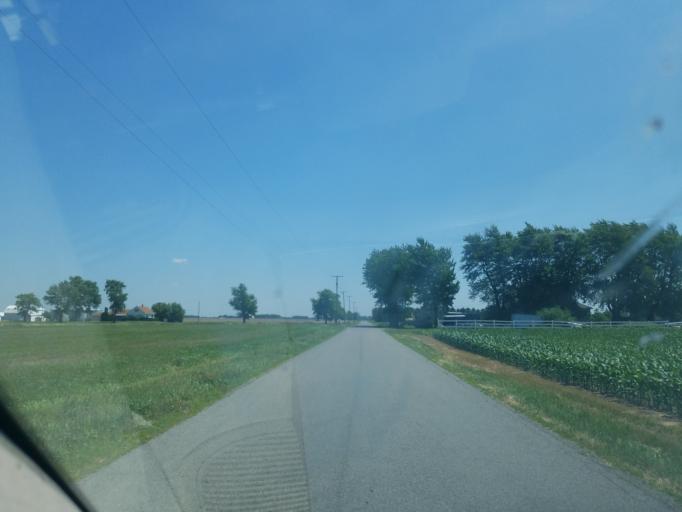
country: US
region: Ohio
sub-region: Allen County
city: Spencerville
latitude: 40.7575
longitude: -84.3720
